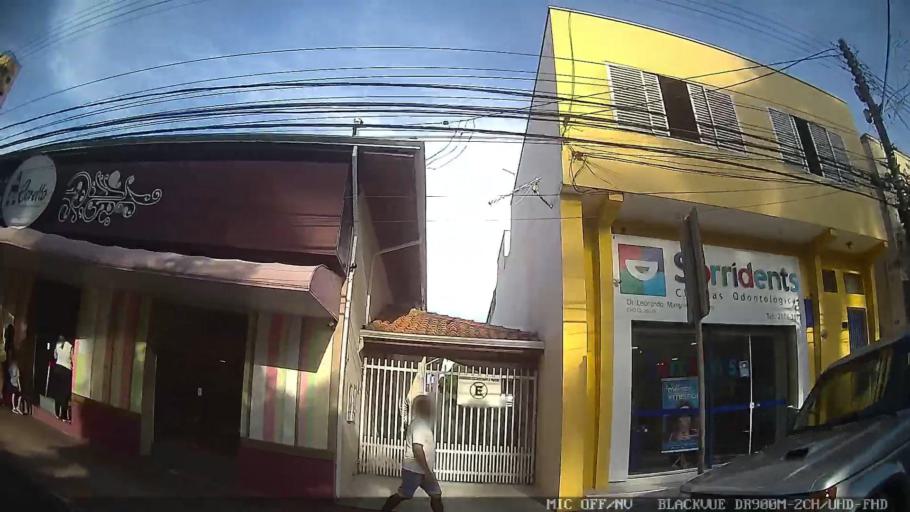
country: BR
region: Sao Paulo
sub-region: Tiete
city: Tiete
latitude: -23.1014
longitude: -47.7143
